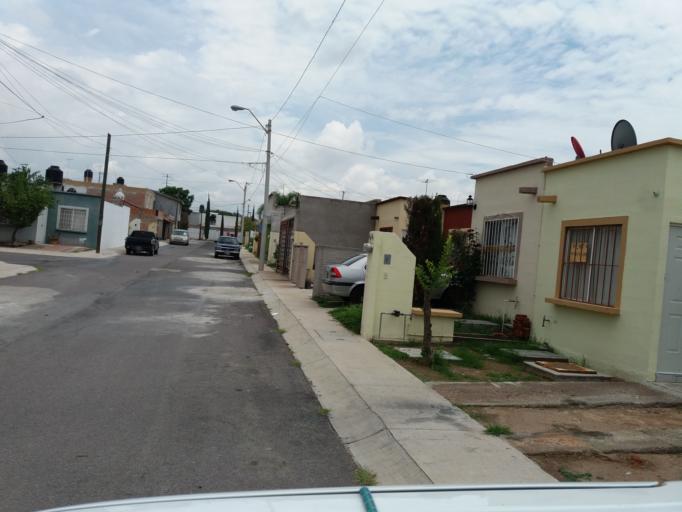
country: MX
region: Aguascalientes
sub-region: Aguascalientes
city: San Sebastian [Fraccionamiento]
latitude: 21.8196
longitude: -102.2690
